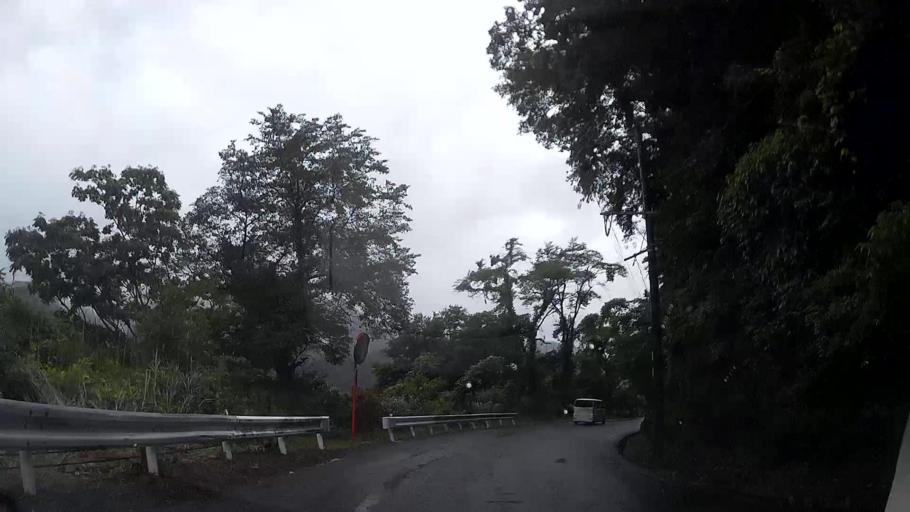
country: JP
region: Oita
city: Hita
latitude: 33.1826
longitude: 130.9986
